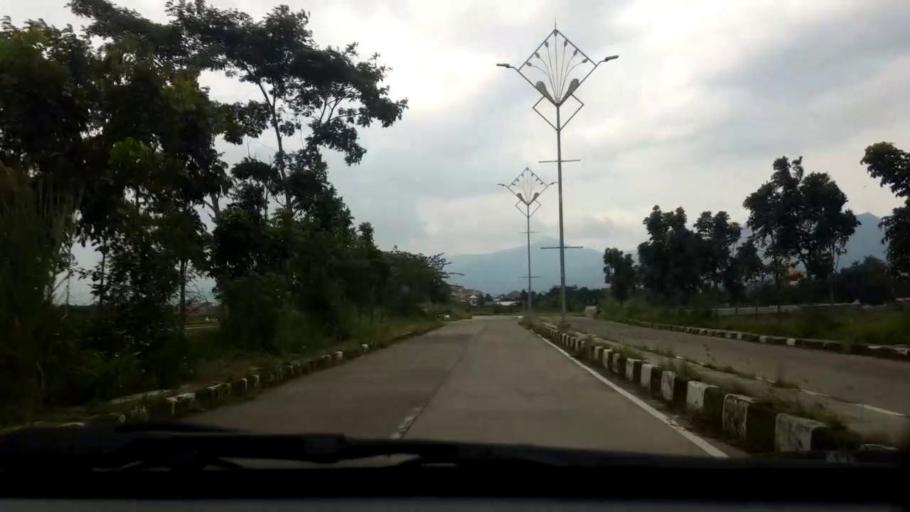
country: ID
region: West Java
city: Cileunyi
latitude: -6.9509
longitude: 107.7111
